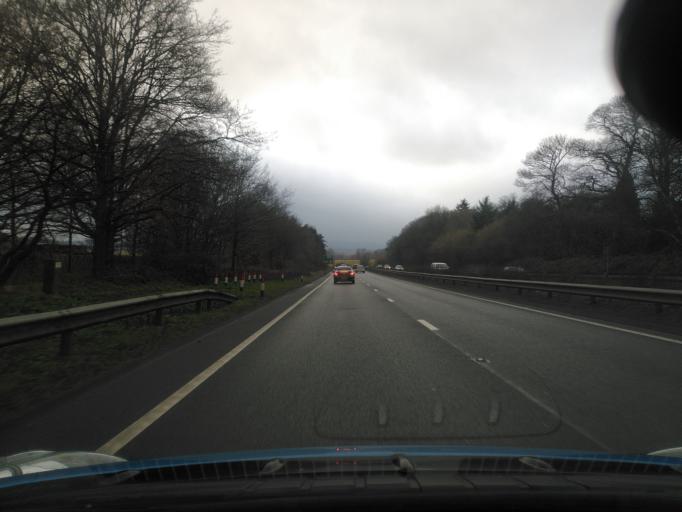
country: GB
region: England
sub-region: Surrey
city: Milford
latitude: 51.1935
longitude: -0.6482
